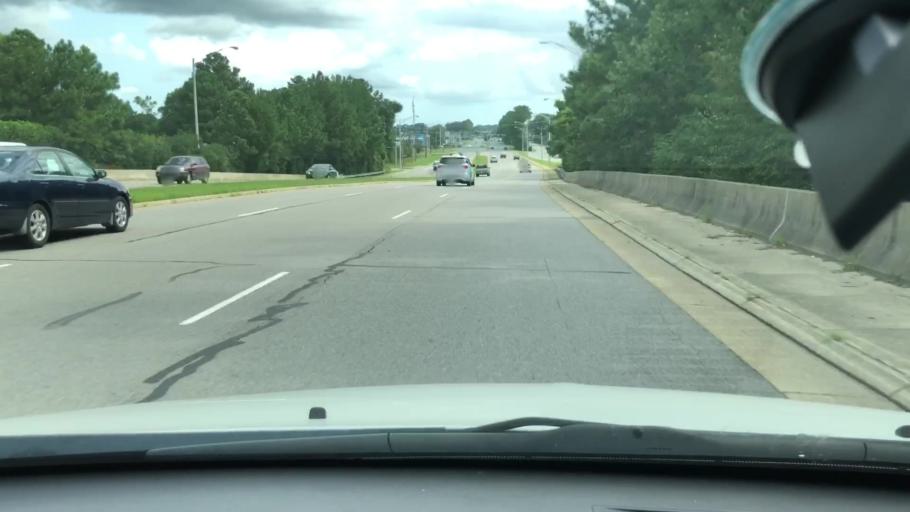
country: US
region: Virginia
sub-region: City of Chesapeake
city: Chesapeake
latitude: 36.7875
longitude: -76.2507
